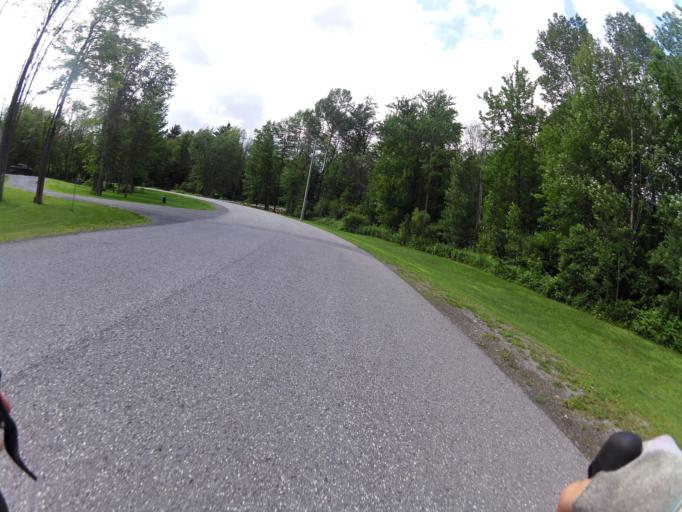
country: CA
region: Ontario
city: Bells Corners
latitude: 45.1724
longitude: -75.8520
